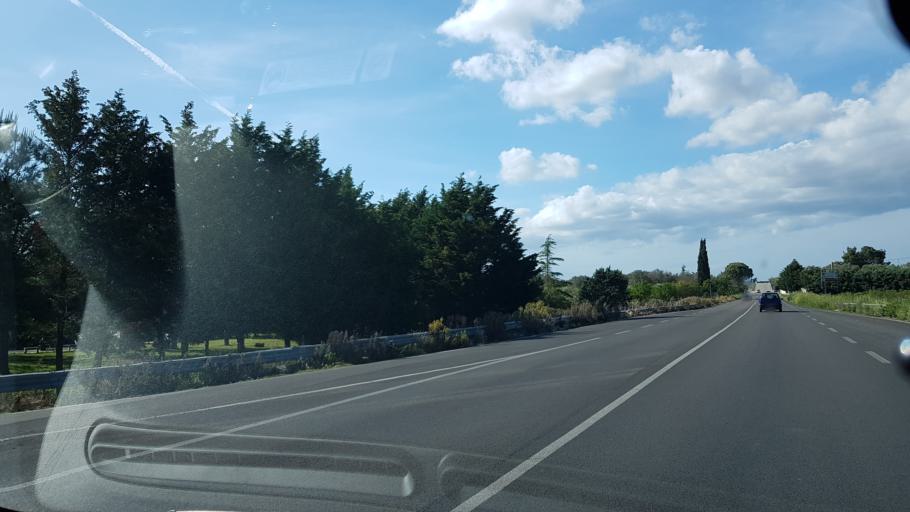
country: IT
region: Apulia
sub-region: Provincia di Brindisi
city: Mesagne
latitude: 40.5626
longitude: 17.7876
